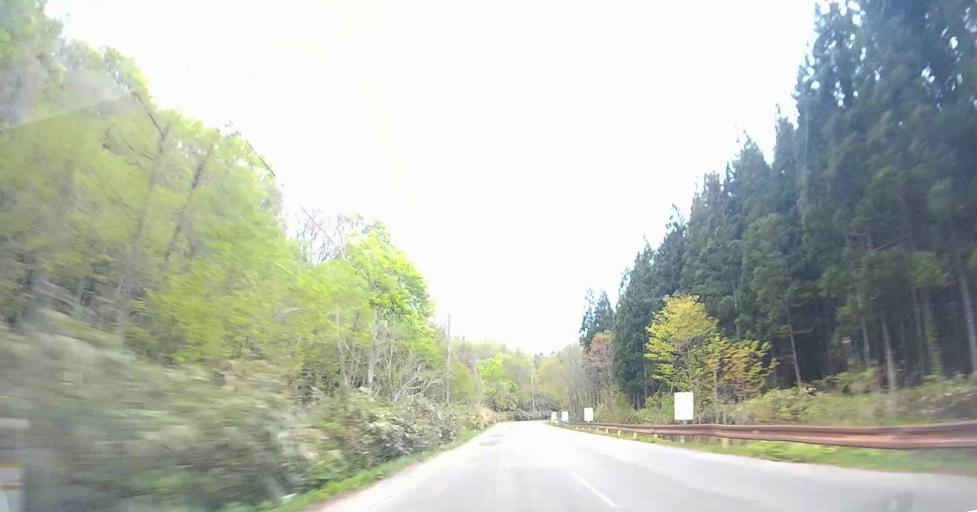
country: JP
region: Aomori
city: Goshogawara
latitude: 41.1160
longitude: 140.5275
